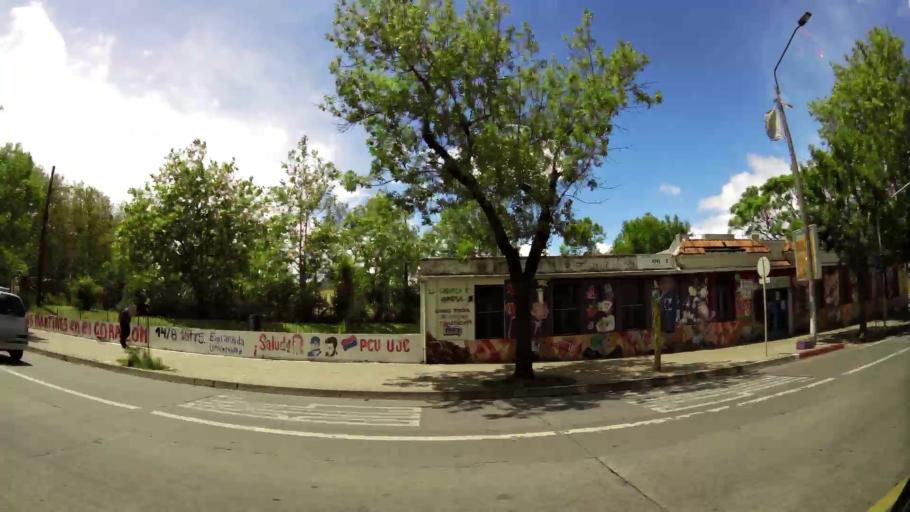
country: UY
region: Montevideo
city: Montevideo
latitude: -34.8686
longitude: -56.1346
